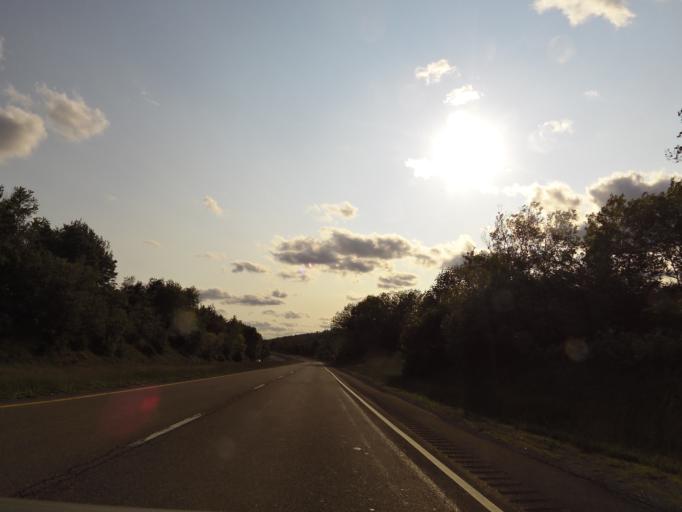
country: US
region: Virginia
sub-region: Tazewell County
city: Claypool Hill
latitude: 37.0877
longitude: -81.6837
